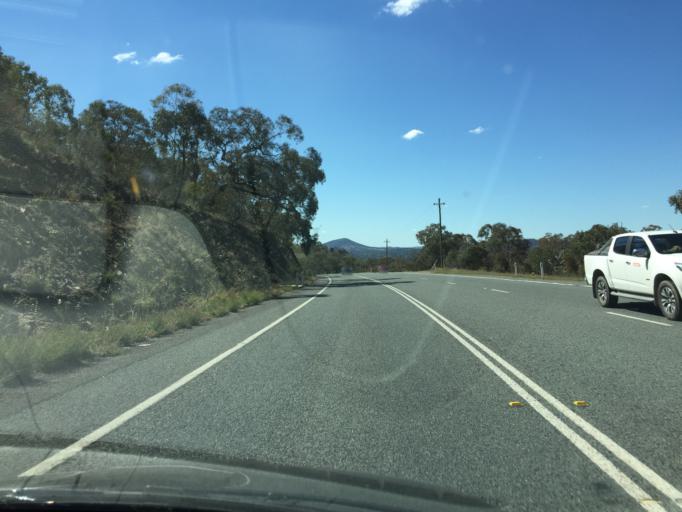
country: AU
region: Australian Capital Territory
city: Macarthur
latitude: -35.4597
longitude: 149.1327
